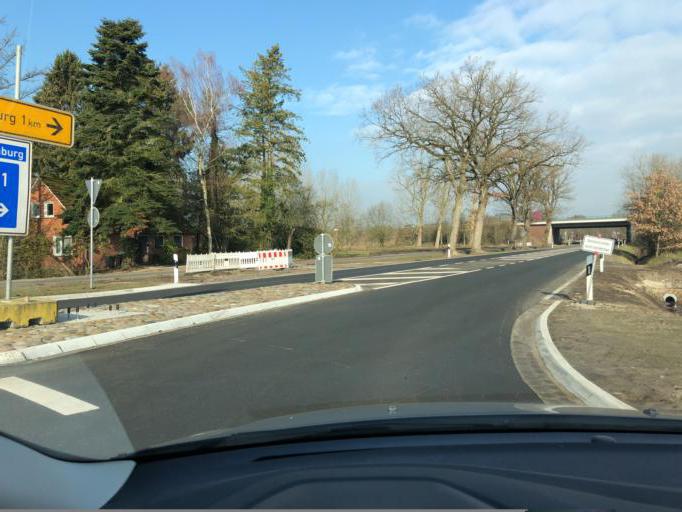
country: DE
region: Lower Saxony
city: Westerstede
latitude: 53.2789
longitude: 7.9016
